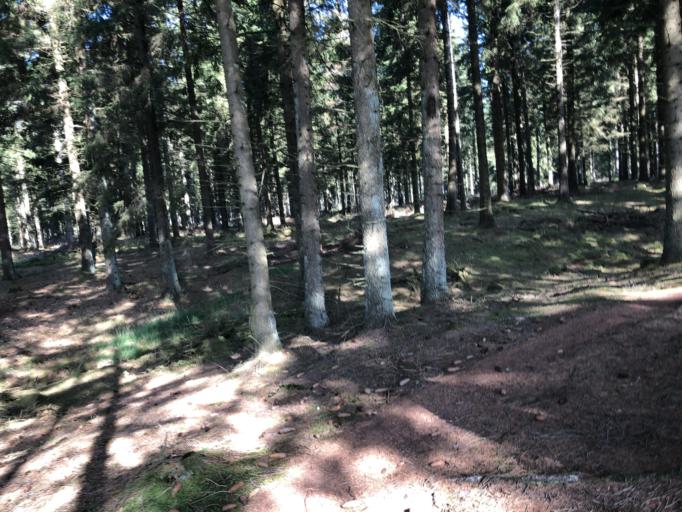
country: DK
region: Central Jutland
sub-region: Lemvig Kommune
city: Lemvig
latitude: 56.4776
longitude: 8.3334
